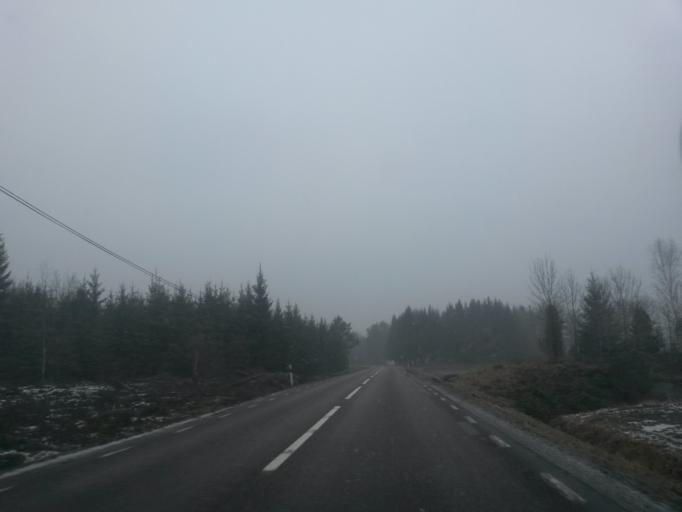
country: SE
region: Vaestra Goetaland
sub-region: Alingsas Kommun
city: Sollebrunn
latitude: 58.2113
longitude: 12.4331
